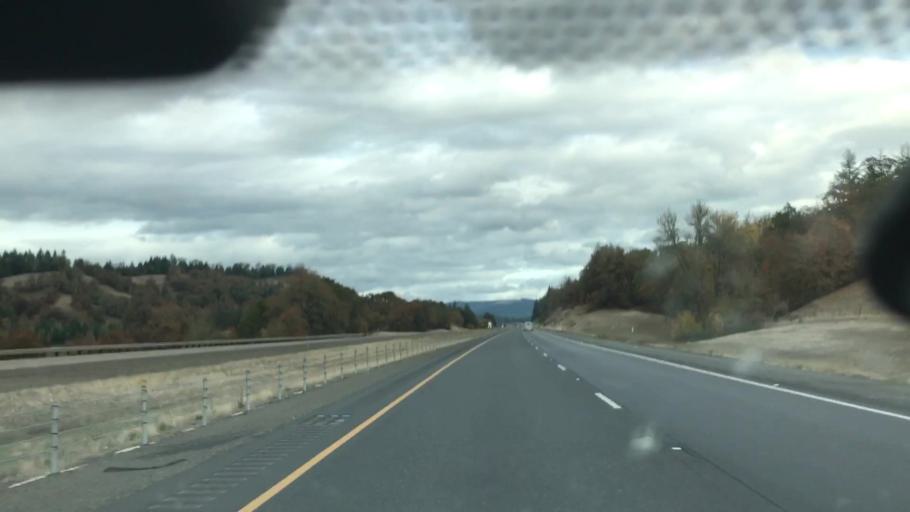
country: US
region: Oregon
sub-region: Douglas County
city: Yoncalla
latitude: 43.5933
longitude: -123.2460
